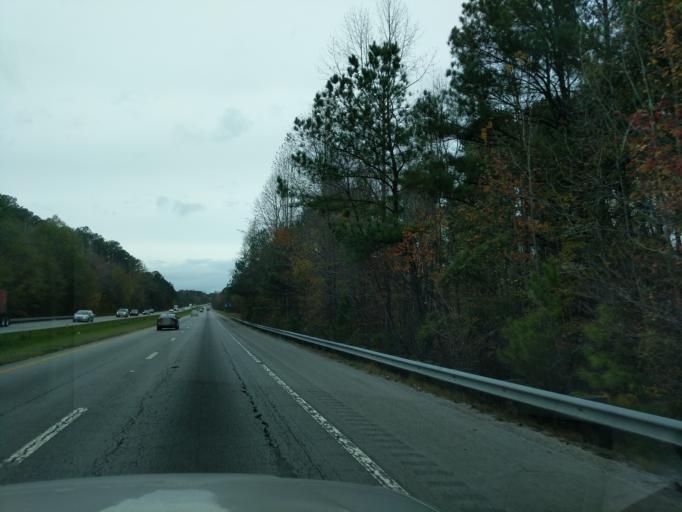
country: US
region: South Carolina
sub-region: Laurens County
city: Joanna
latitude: 34.4337
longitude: -81.7461
